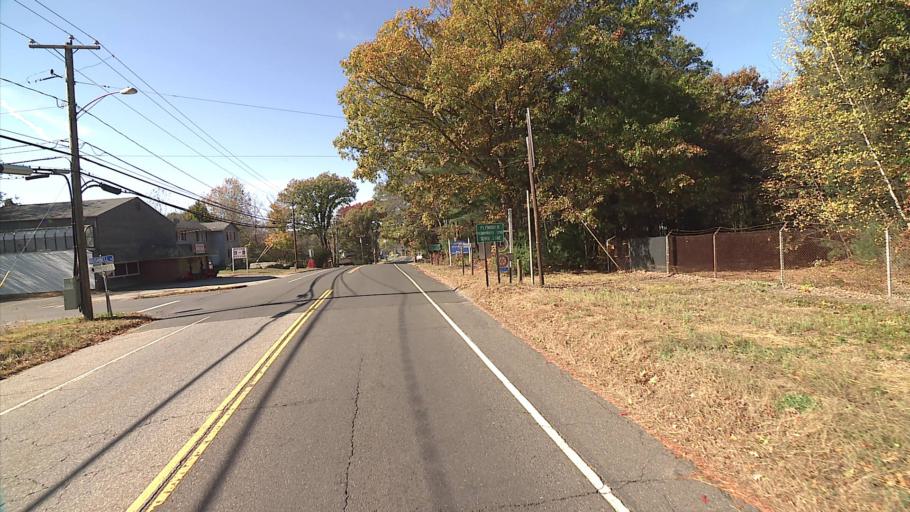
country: US
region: Connecticut
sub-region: Litchfield County
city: Terryville
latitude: 41.6800
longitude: -72.9913
